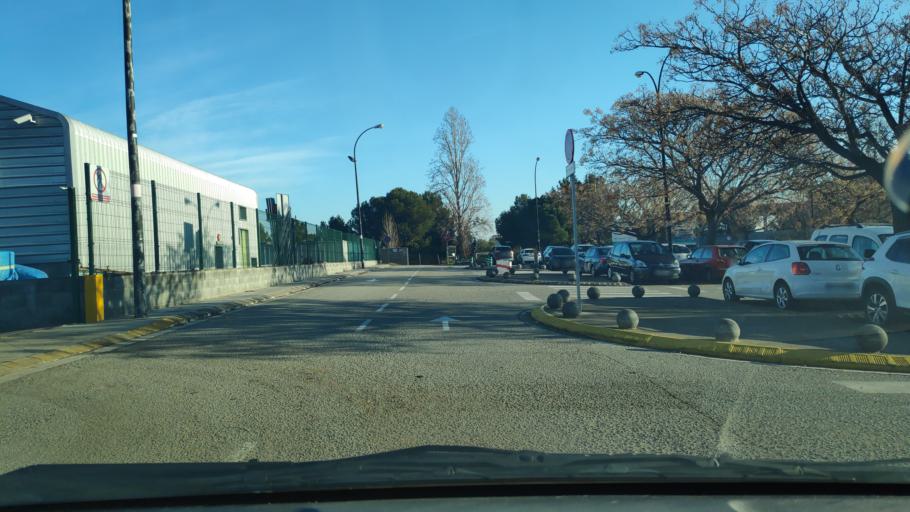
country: ES
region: Catalonia
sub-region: Provincia de Barcelona
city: Barbera del Valles
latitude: 41.5035
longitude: 2.1096
